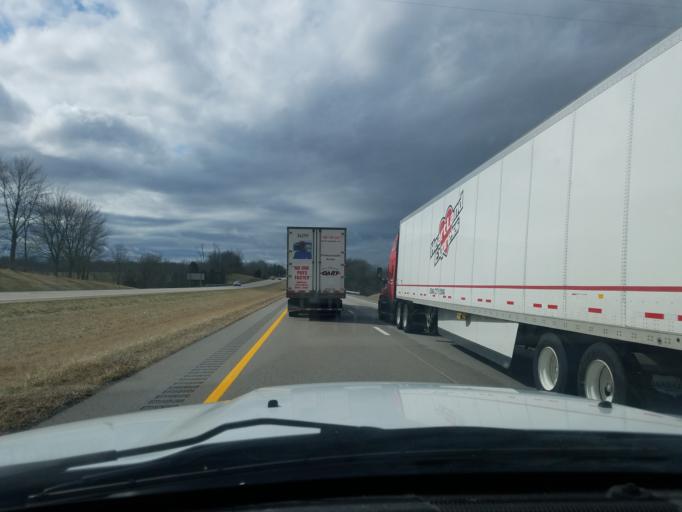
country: US
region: Kentucky
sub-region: Montgomery County
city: Mount Sterling
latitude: 38.0927
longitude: -83.8756
